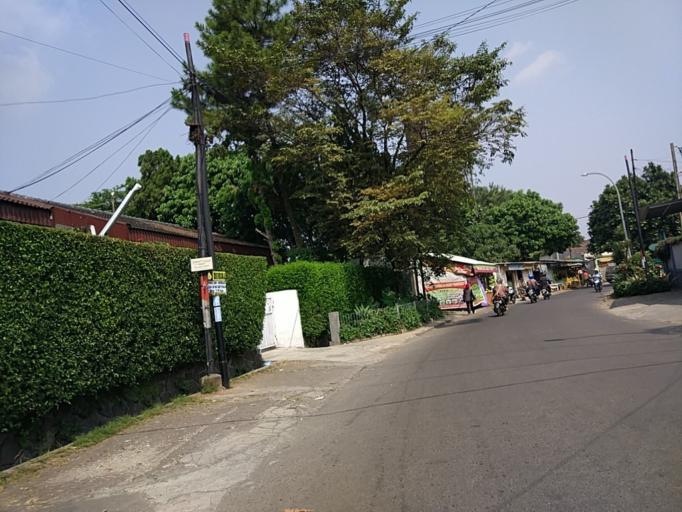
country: ID
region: West Java
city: Margahayukencana
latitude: -6.9338
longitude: 107.5758
